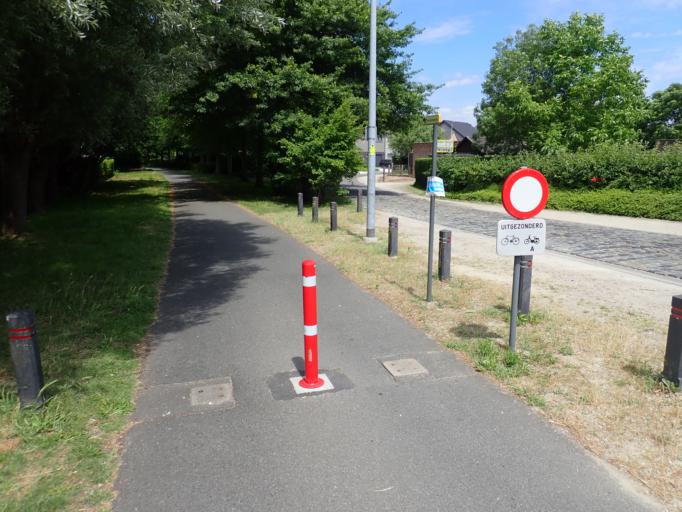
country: BE
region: Flanders
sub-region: Provincie Oost-Vlaanderen
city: Hamme
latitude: 51.0899
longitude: 4.1320
